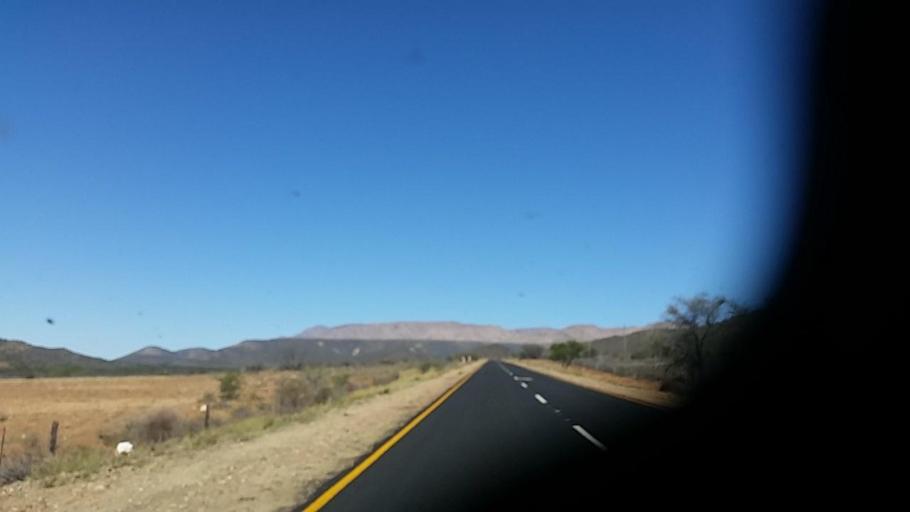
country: ZA
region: Western Cape
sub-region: Eden District Municipality
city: George
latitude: -33.5417
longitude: 22.7275
